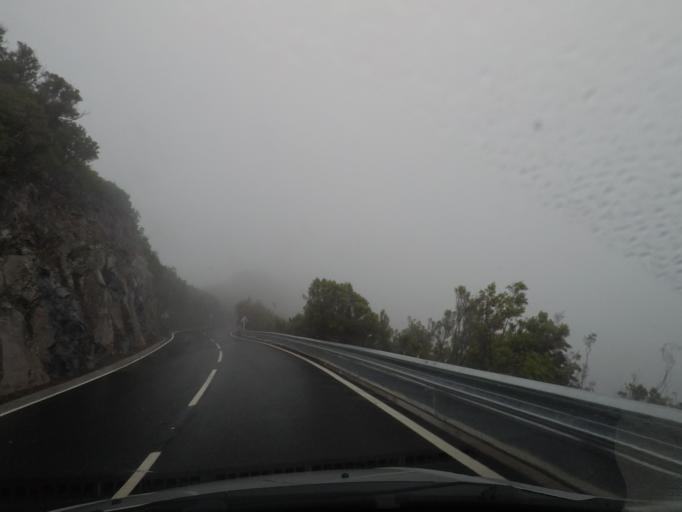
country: PT
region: Madeira
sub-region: Santana
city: Santana
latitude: 32.7707
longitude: -16.9177
